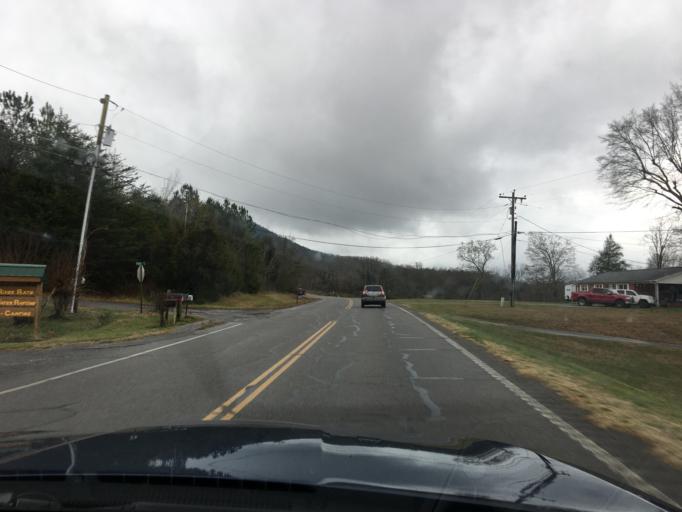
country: US
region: Tennessee
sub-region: Polk County
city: Benton
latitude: 35.1097
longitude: -84.6560
